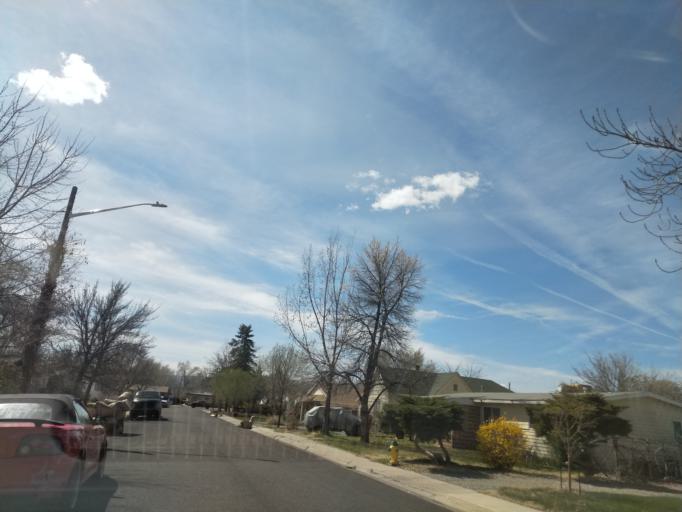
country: US
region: Colorado
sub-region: Mesa County
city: Grand Junction
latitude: 39.0831
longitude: -108.5465
